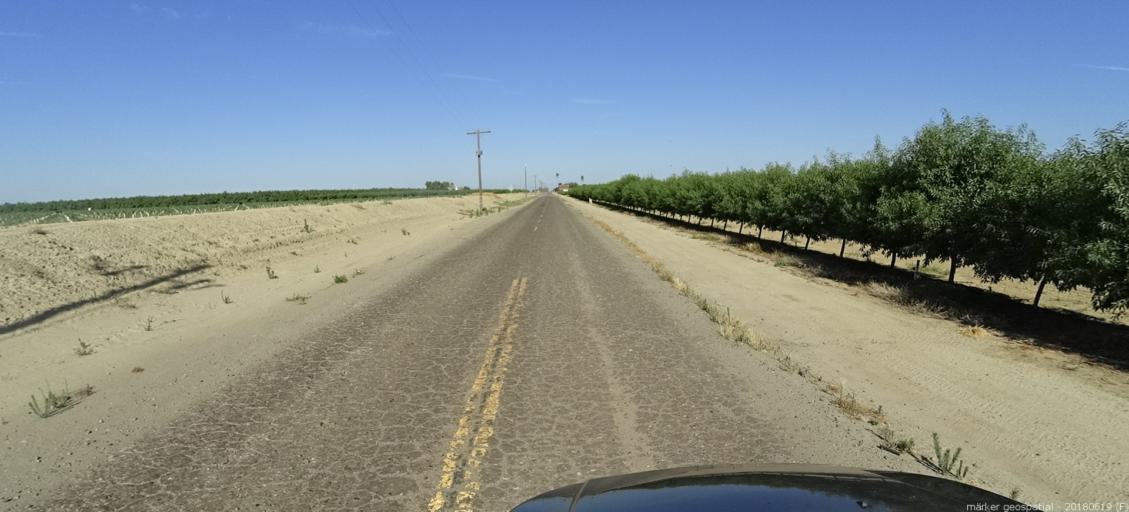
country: US
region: California
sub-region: Fresno County
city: Biola
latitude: 36.8296
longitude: -120.0255
